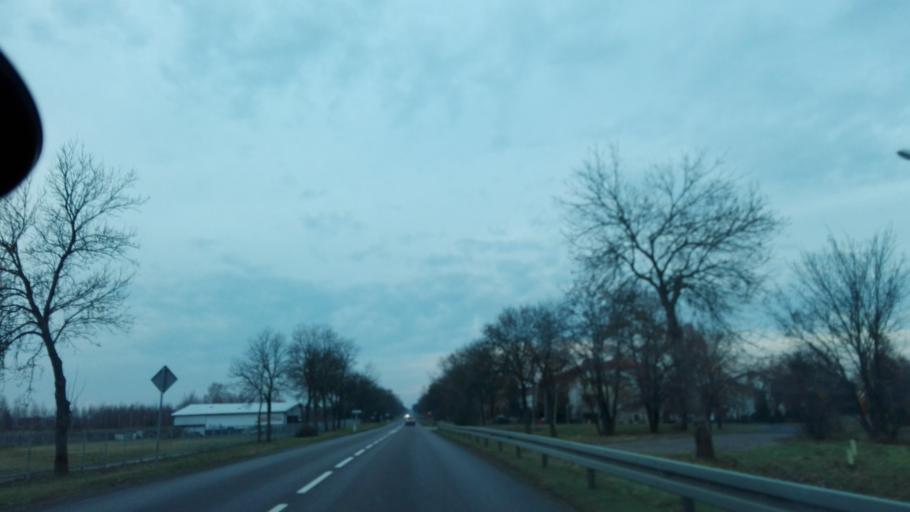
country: PL
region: Lublin Voivodeship
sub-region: Powiat radzynski
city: Radzyn Podlaski
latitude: 51.7754
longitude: 22.6437
